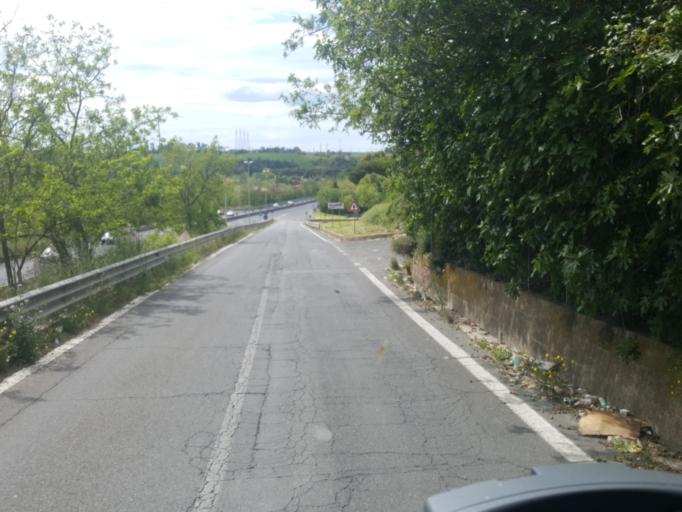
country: IT
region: Latium
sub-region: Citta metropolitana di Roma Capitale
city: La Massimina-Casal Lumbroso
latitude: 41.8826
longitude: 12.3436
